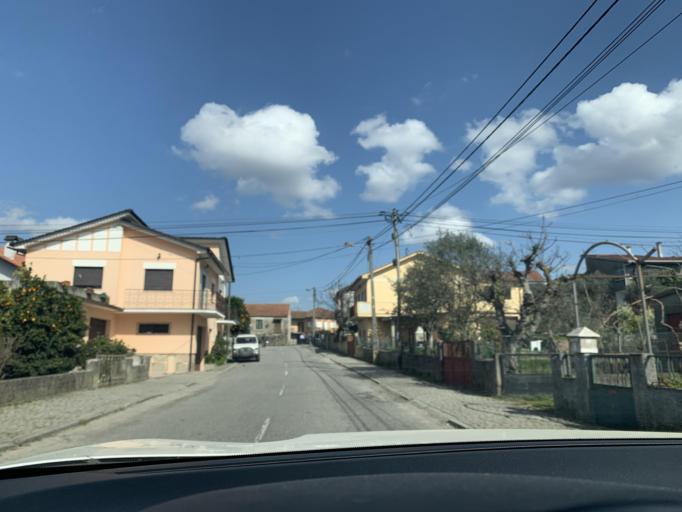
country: PT
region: Viseu
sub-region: Viseu
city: Rio de Loba
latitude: 40.6706
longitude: -7.8797
